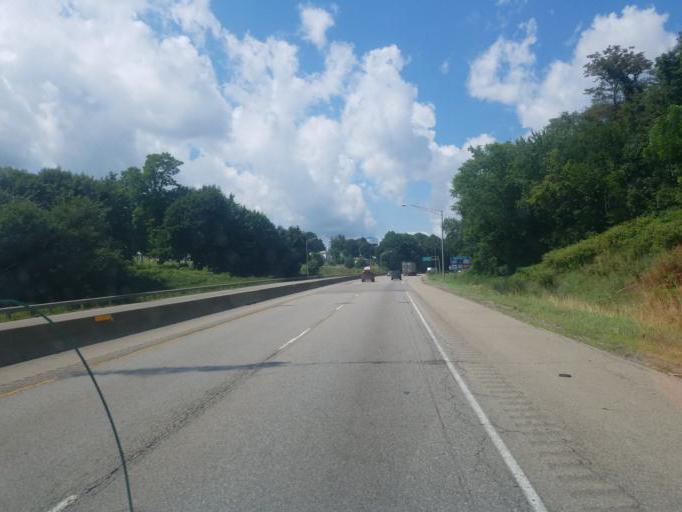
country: US
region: Ohio
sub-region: Muskingum County
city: Zanesville
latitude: 39.9452
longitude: -81.9864
